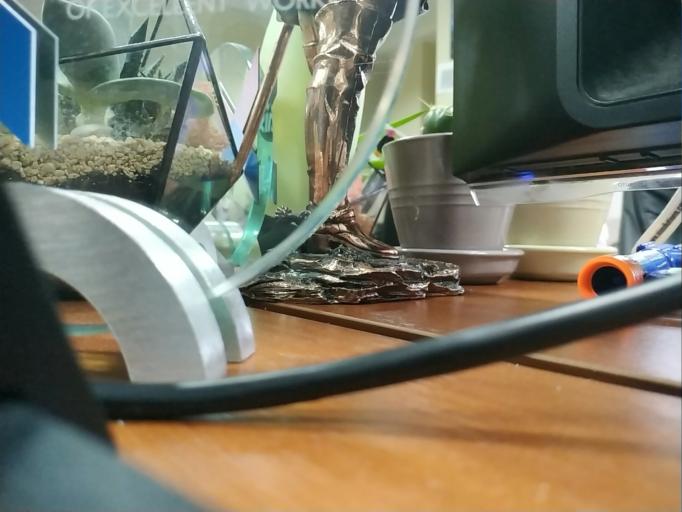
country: RU
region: Moskovskaya
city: Lugovaya
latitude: 56.0661
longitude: 37.4658
